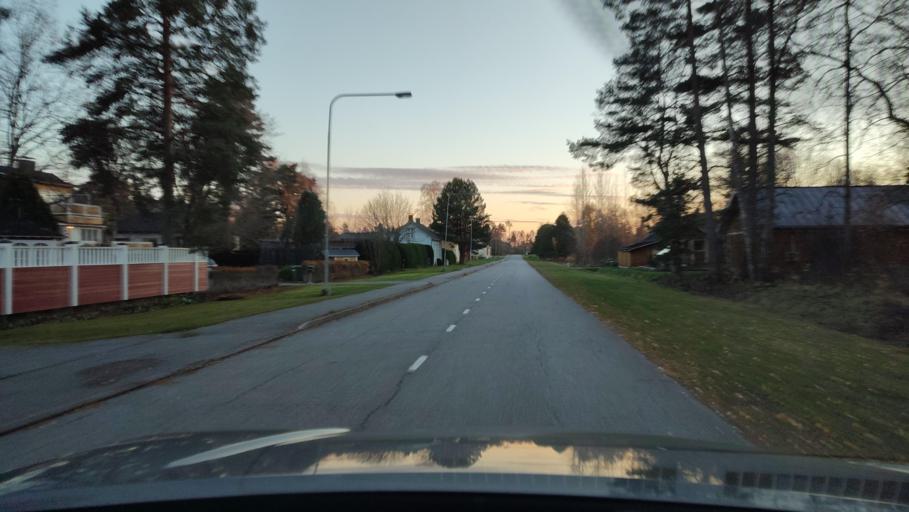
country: FI
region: Ostrobothnia
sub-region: Sydosterbotten
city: Kristinestad
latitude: 62.2702
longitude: 21.3915
